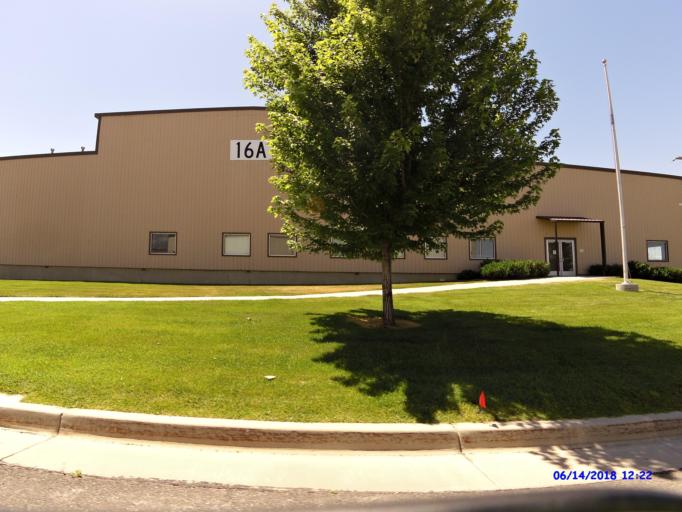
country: US
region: Utah
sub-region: Weber County
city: Marriott-Slaterville
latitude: 41.2628
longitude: -112.0066
